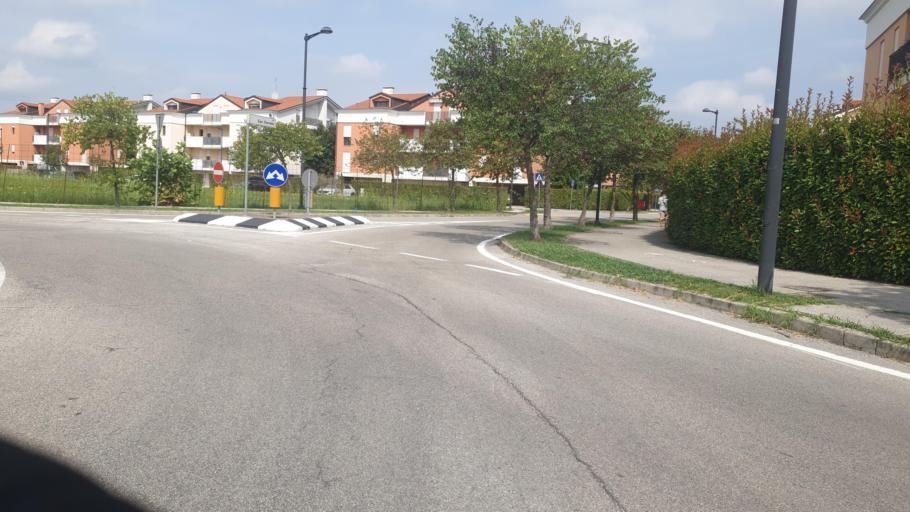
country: IT
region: Veneto
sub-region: Provincia di Padova
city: Albignasego
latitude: 45.3377
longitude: 11.8758
